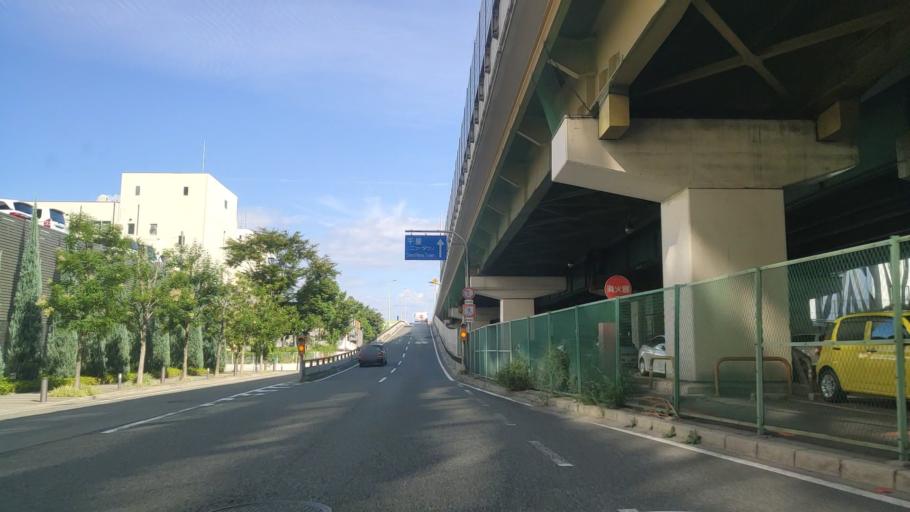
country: JP
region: Osaka
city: Suita
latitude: 34.7463
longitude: 135.4975
